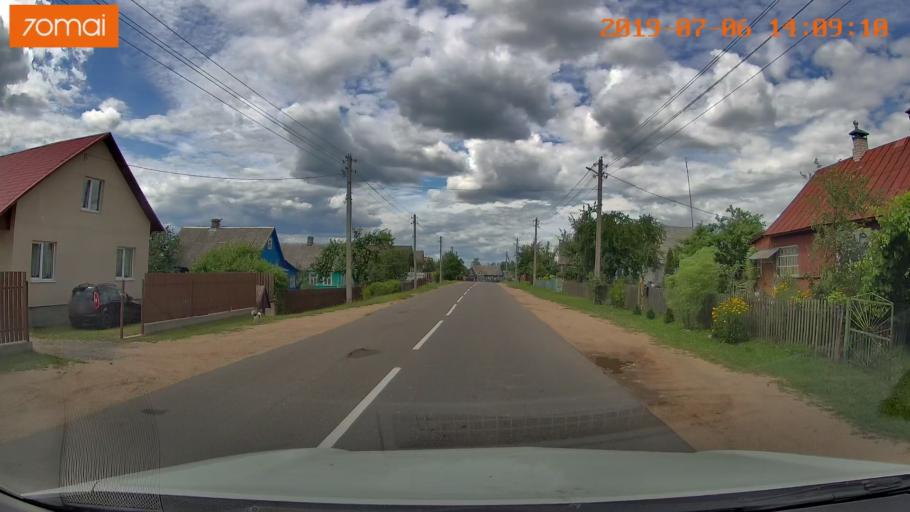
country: BY
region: Minsk
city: Ivyanyets
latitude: 53.8799
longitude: 26.7501
